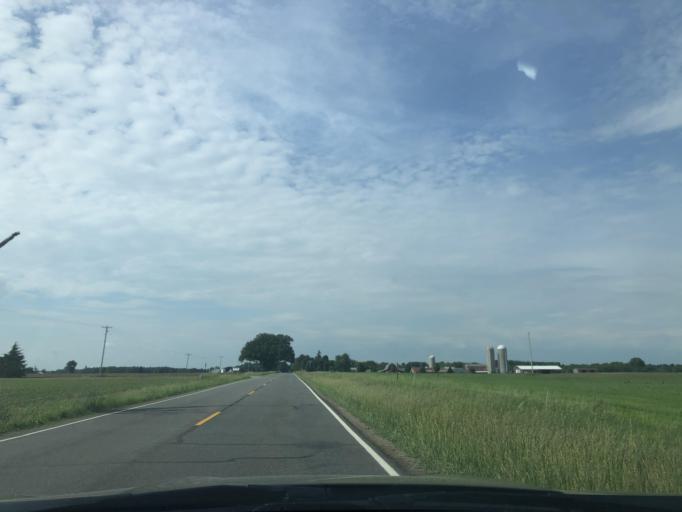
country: US
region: Michigan
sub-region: Clinton County
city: Bath
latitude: 42.8265
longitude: -84.4838
